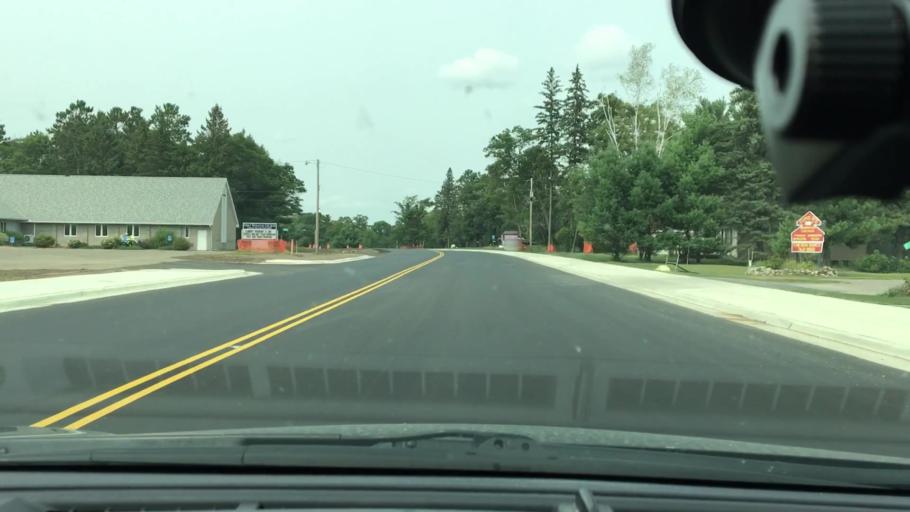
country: US
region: Minnesota
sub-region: Crow Wing County
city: Cross Lake
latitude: 46.7326
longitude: -93.9579
